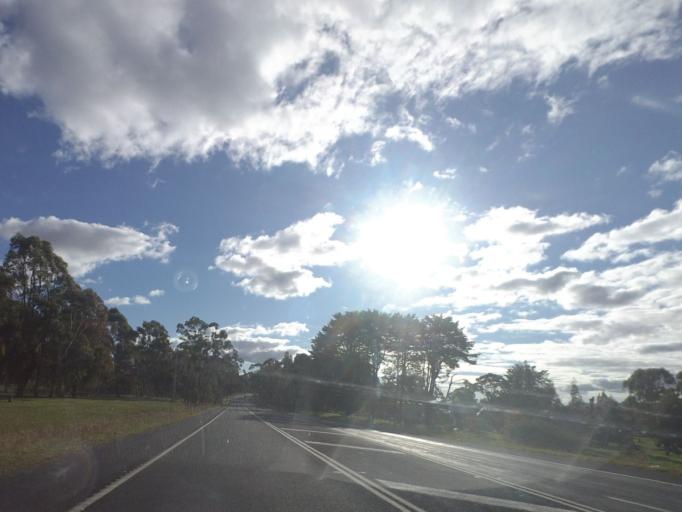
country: AU
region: Victoria
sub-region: Mount Alexander
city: Castlemaine
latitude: -37.0996
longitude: 144.3325
